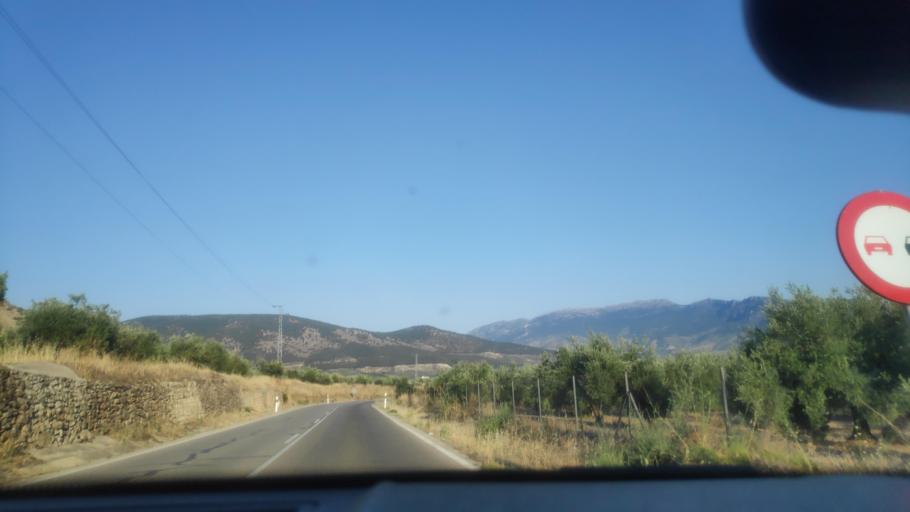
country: ES
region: Andalusia
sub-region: Provincia de Jaen
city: Jaen
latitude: 37.7466
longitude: -3.7807
